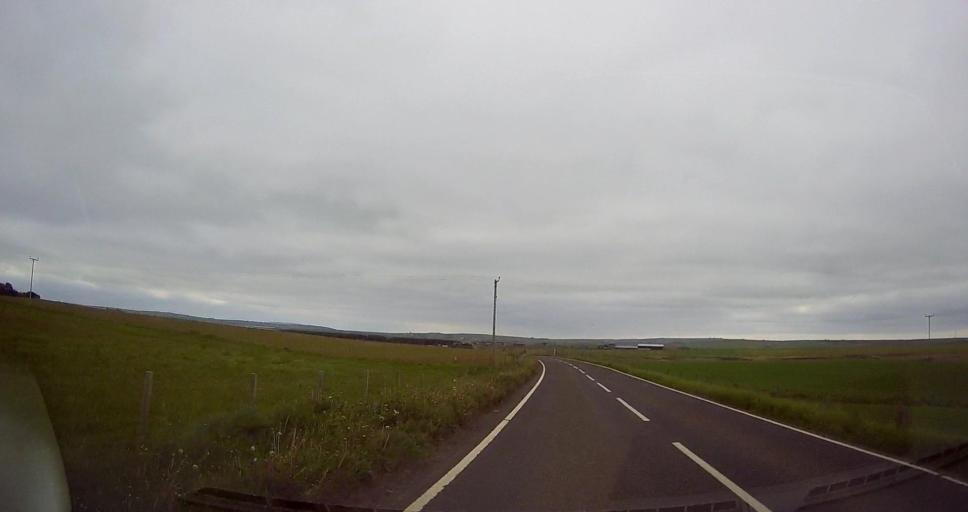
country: GB
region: Scotland
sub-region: Orkney Islands
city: Kirkwall
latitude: 58.9420
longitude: -2.8723
